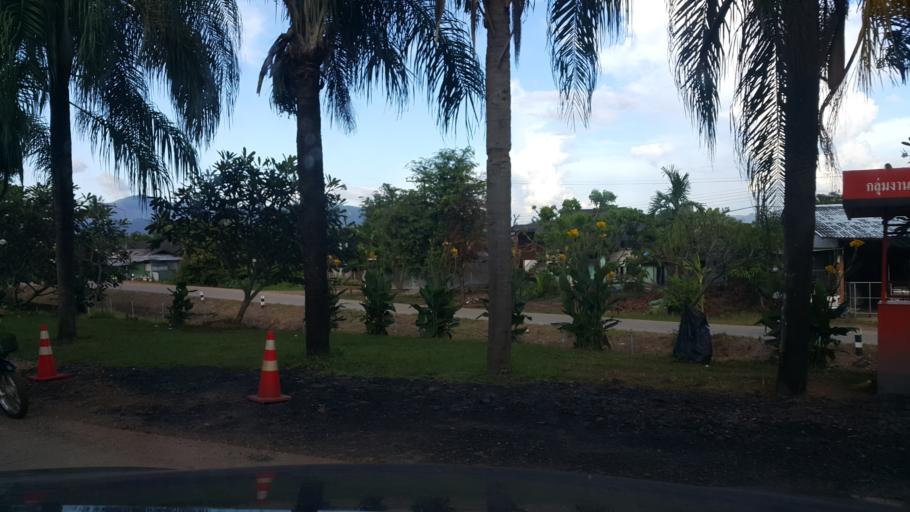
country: TH
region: Chiang Mai
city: Mae Taeng
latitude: 19.1578
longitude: 98.9797
